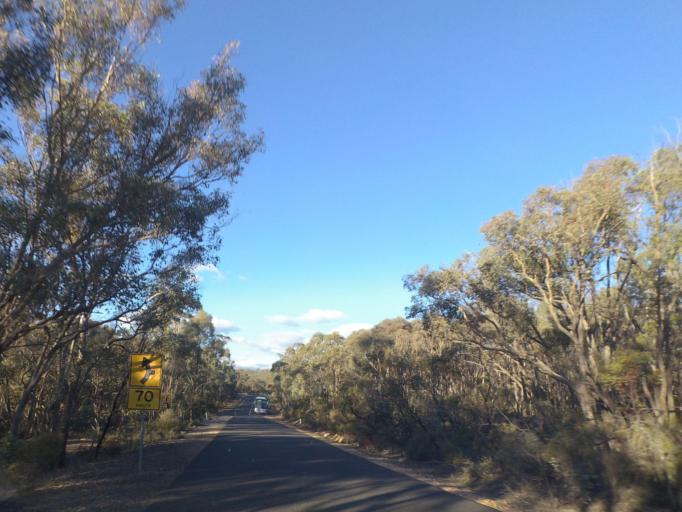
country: AU
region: Victoria
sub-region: Mount Alexander
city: Castlemaine
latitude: -37.1561
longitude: 144.2282
